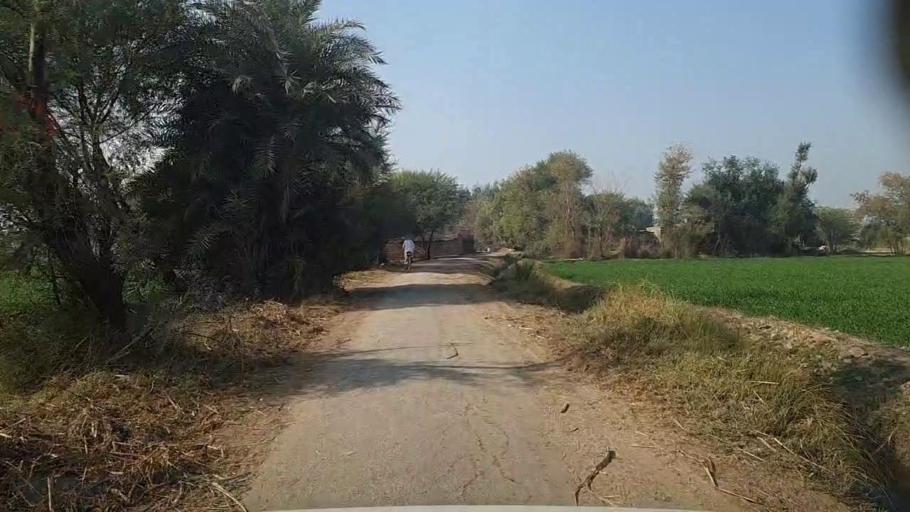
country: PK
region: Sindh
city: Khairpur
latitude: 27.9220
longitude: 69.6631
